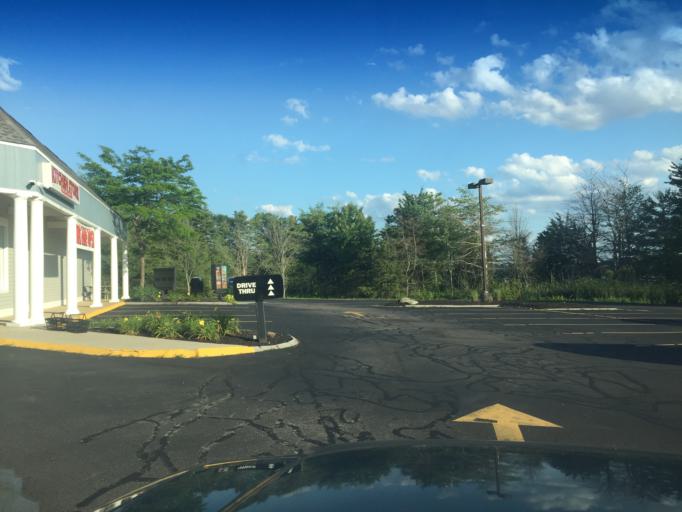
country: US
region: Maine
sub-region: York County
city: Kittery
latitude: 43.1138
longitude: -70.7308
